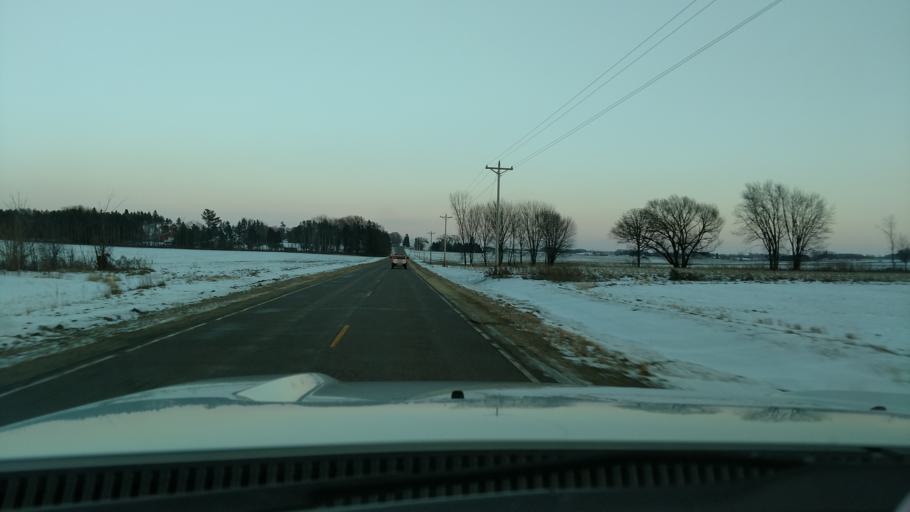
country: US
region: Wisconsin
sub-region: Saint Croix County
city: Hammond
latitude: 44.9132
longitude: -92.4979
